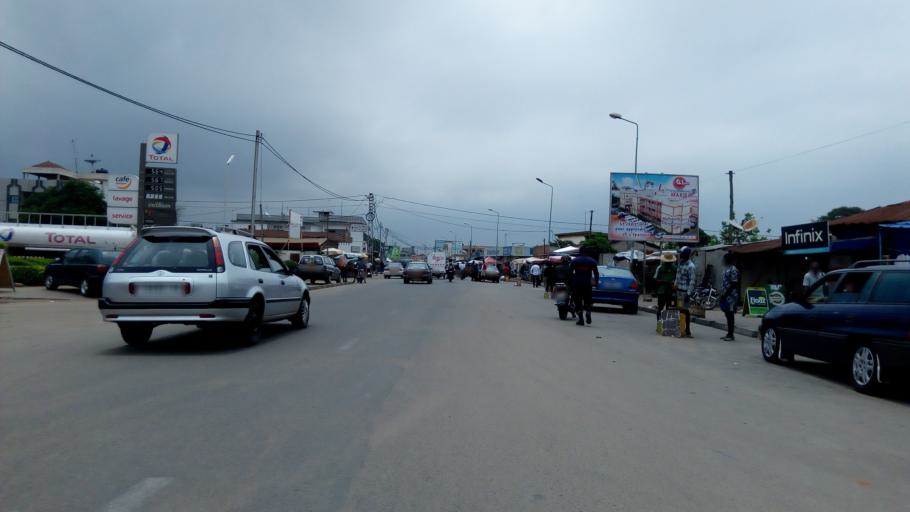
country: TG
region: Maritime
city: Lome
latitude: 6.1382
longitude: 1.2294
